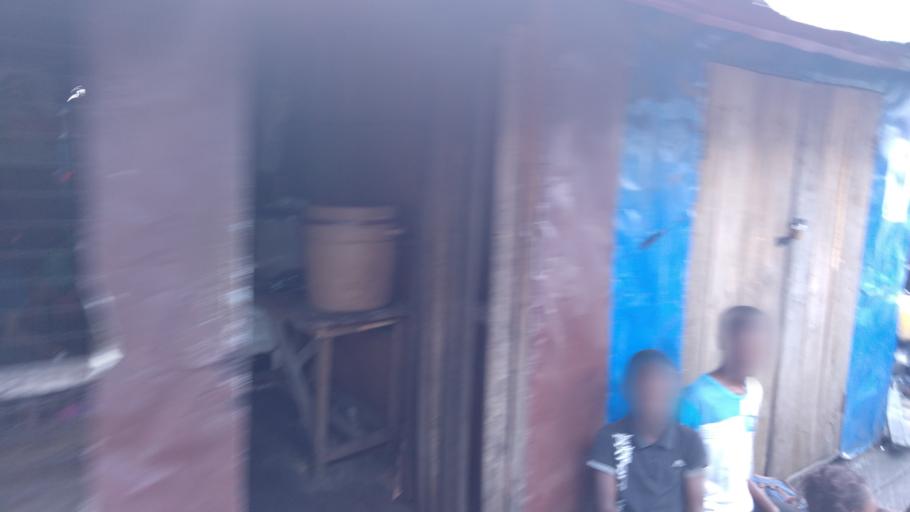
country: NG
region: Ondo
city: Igbekebo
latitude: 5.9200
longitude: 4.9675
